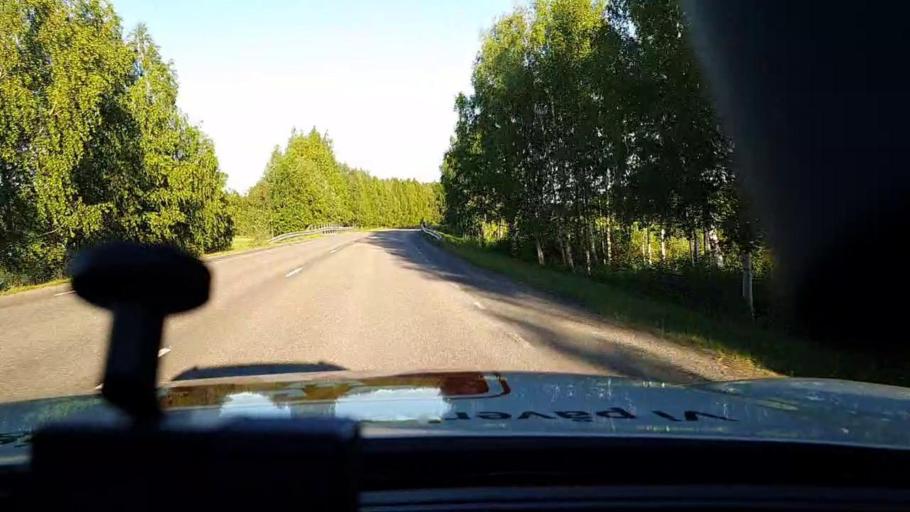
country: SE
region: Norrbotten
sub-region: Lulea Kommun
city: Lulea
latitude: 65.6125
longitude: 22.1604
